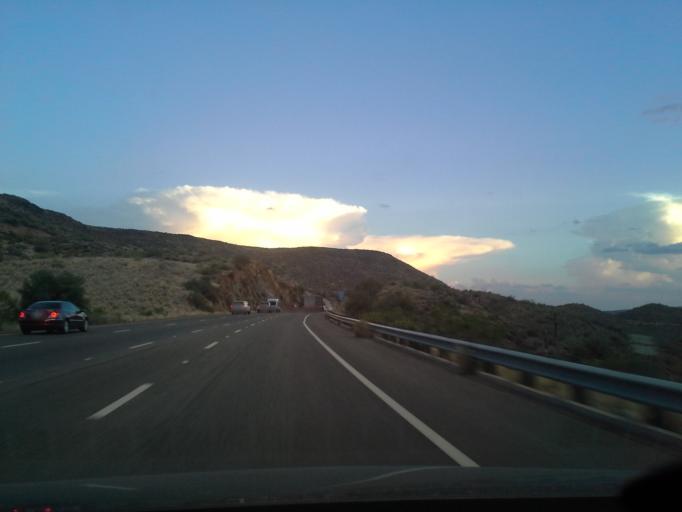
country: US
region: Arizona
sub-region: Yavapai County
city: Black Canyon City
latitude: 34.1376
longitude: -112.1484
